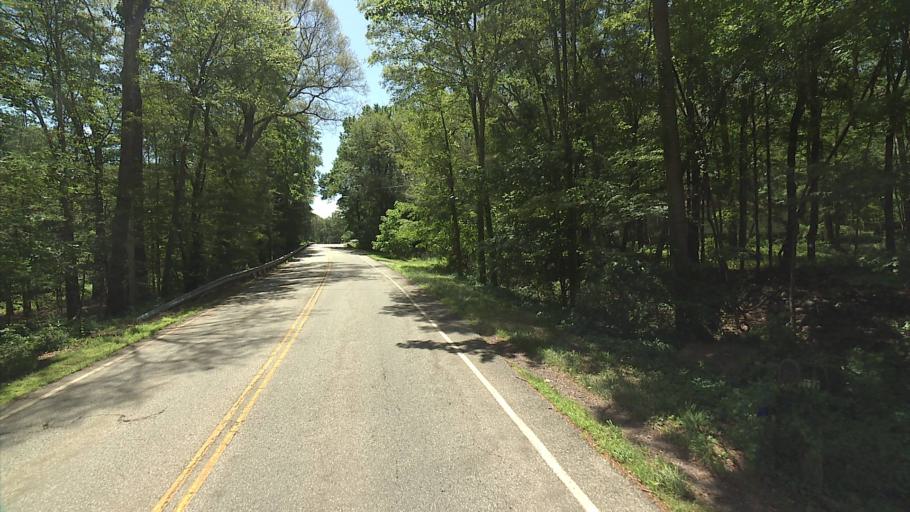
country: US
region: Connecticut
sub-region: Middlesex County
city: East Hampton
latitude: 41.5457
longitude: -72.5057
